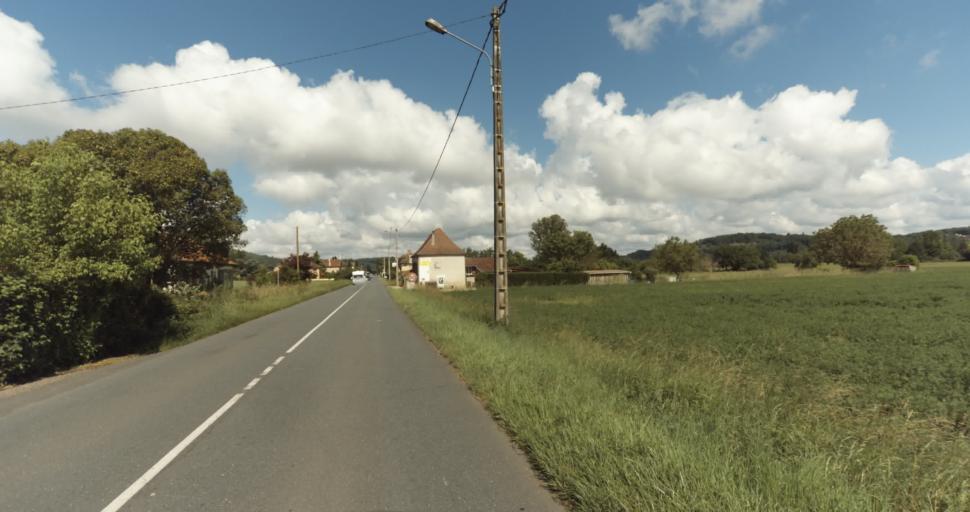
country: FR
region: Aquitaine
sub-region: Departement de la Dordogne
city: Le Bugue
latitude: 44.8445
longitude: 0.9211
